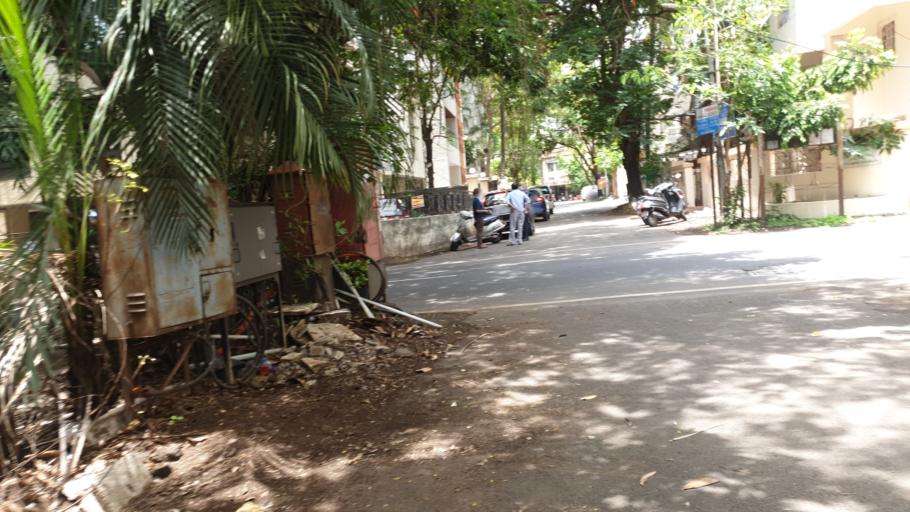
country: IN
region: Maharashtra
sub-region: Pune Division
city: Pune
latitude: 18.4922
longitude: 73.8272
